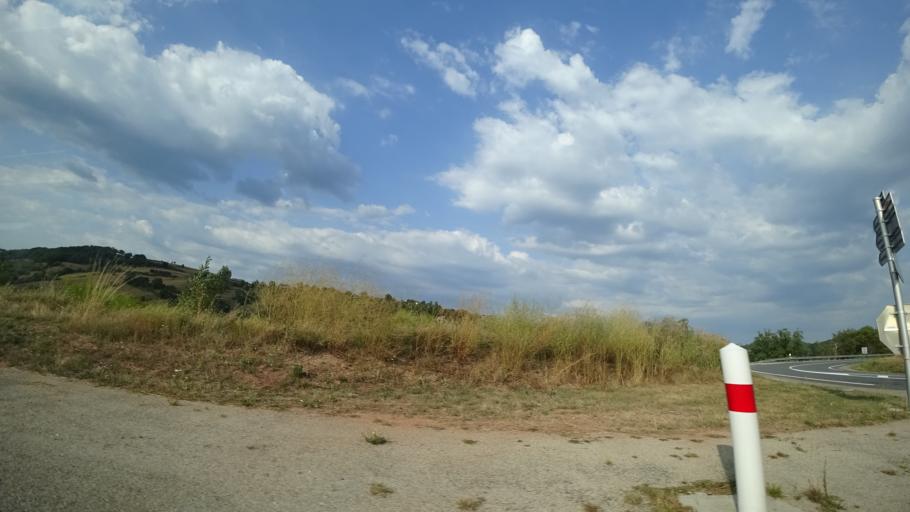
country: FR
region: Midi-Pyrenees
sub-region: Departement de l'Aveyron
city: Firmi
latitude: 44.5139
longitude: 2.3577
